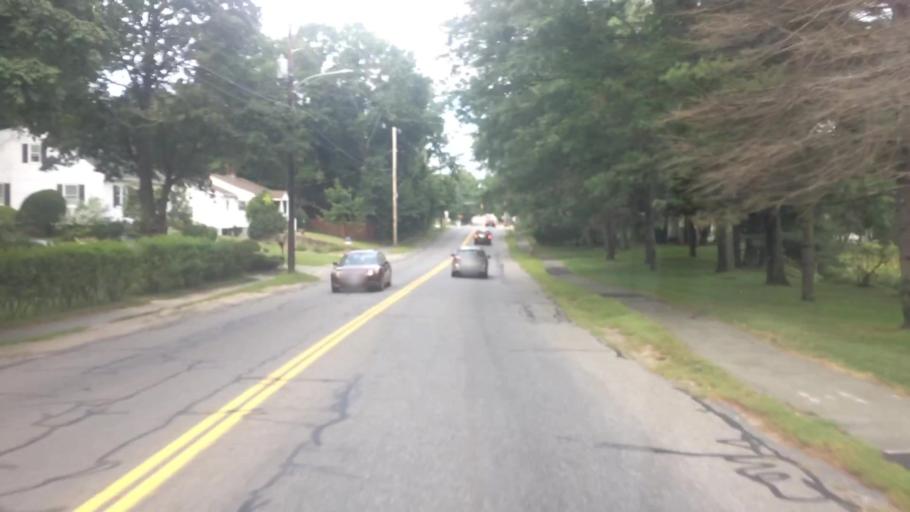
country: US
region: Massachusetts
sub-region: Middlesex County
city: West Concord
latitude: 42.4560
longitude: -71.3852
